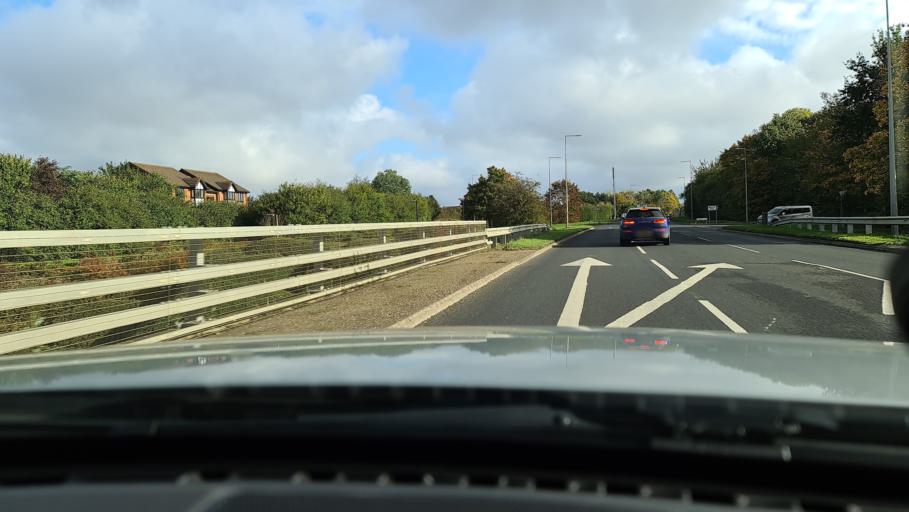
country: GB
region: England
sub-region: Milton Keynes
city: Simpson
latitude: 52.0245
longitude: -0.6961
